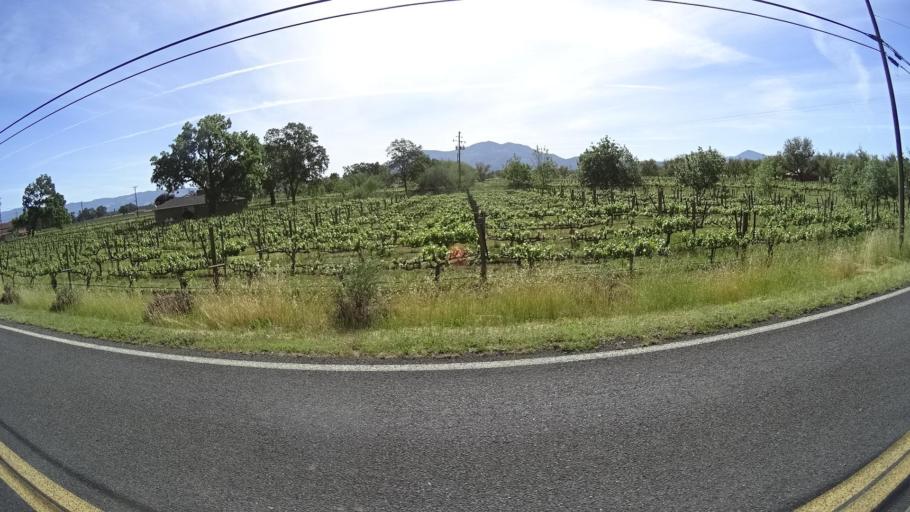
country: US
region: California
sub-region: Lake County
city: Kelseyville
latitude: 38.9818
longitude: -122.8944
